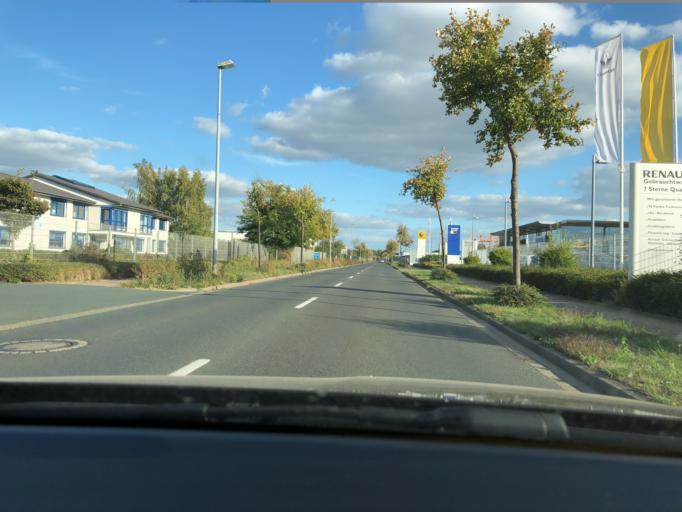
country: DE
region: Lower Saxony
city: Stuhr
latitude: 53.0244
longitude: 8.7634
